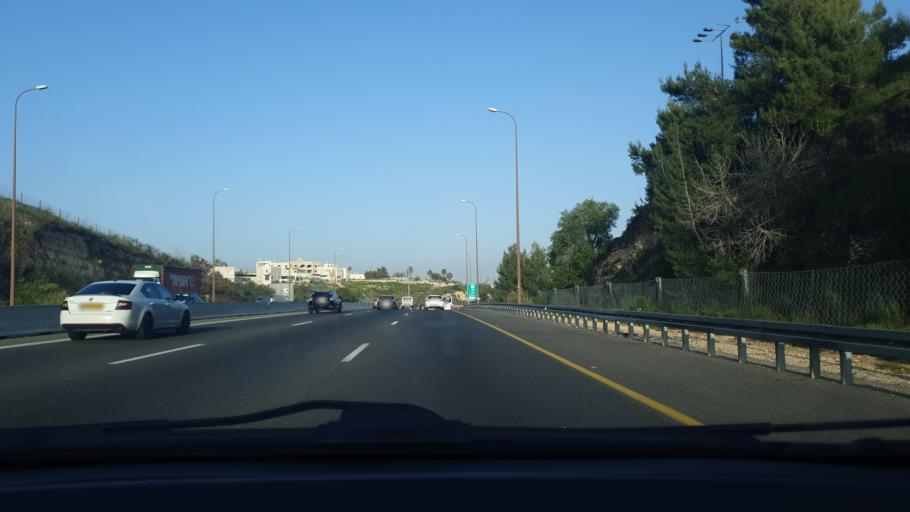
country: IL
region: Jerusalem
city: Abu Ghaush
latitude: 31.8015
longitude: 35.1051
